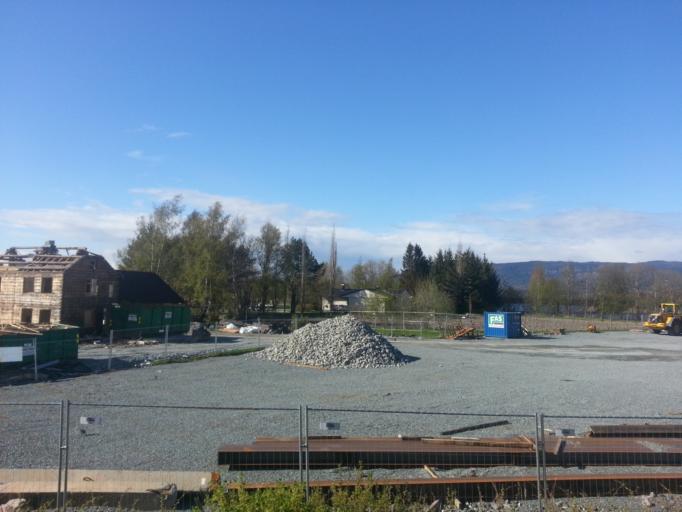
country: NO
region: Nord-Trondelag
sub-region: Stjordal
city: Stjordal
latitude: 63.4464
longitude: 10.9036
